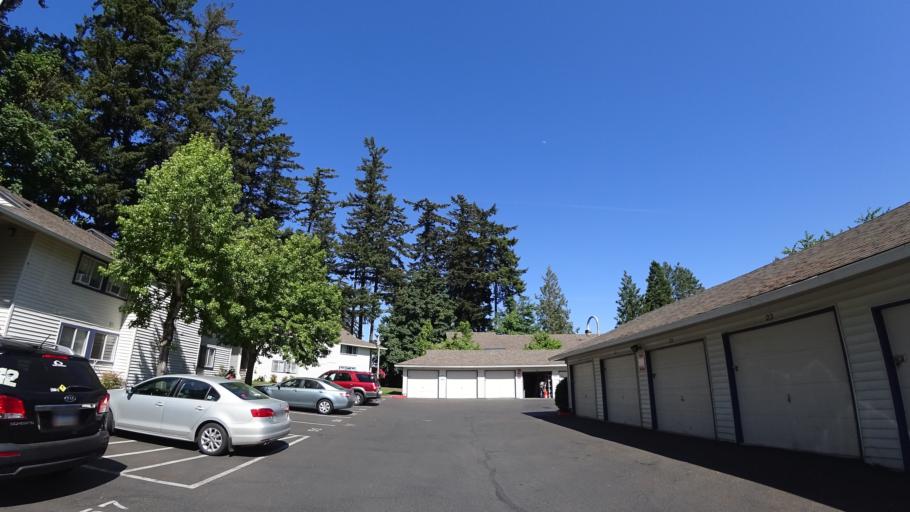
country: US
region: Oregon
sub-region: Multnomah County
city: Gresham
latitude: 45.4897
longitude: -122.4787
